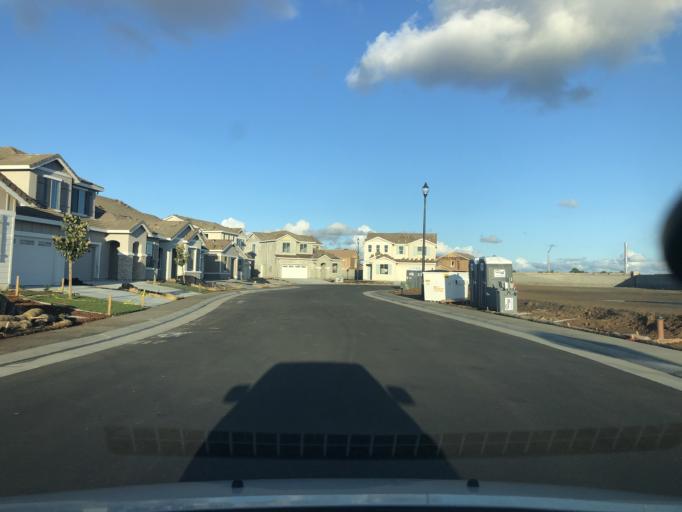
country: US
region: California
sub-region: Sacramento County
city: Antelope
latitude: 38.7601
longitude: -121.3658
